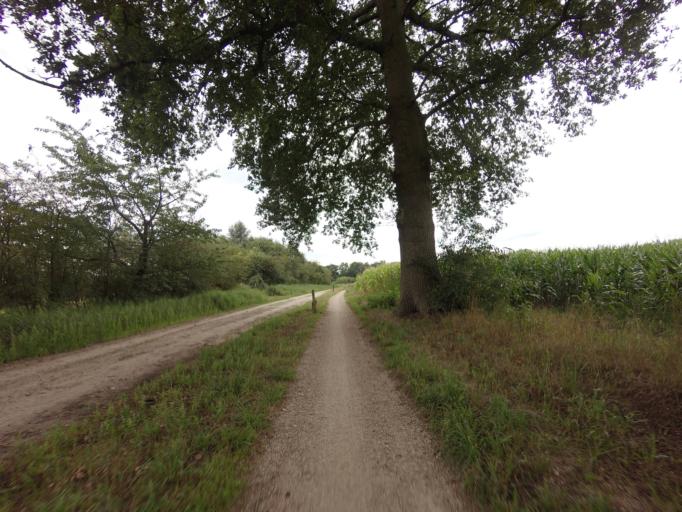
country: NL
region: Gelderland
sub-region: Gemeente Lochem
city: Laren
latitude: 52.2953
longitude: 6.3962
